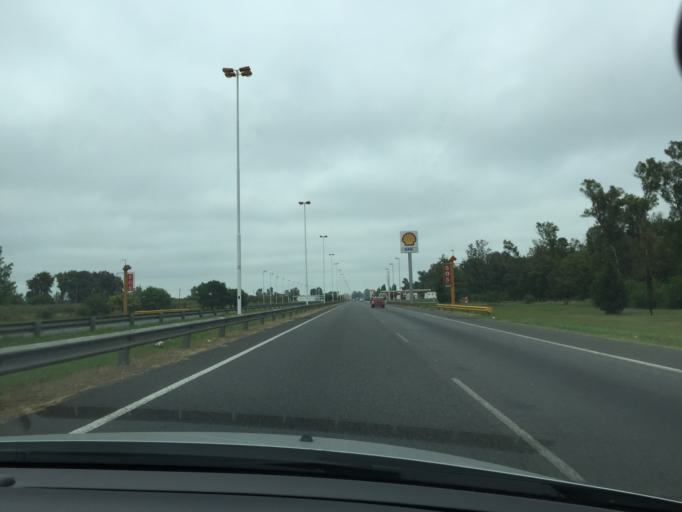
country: AR
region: Buenos Aires
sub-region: Partido de Ezeiza
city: Ezeiza
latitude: -34.8583
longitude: -58.5602
